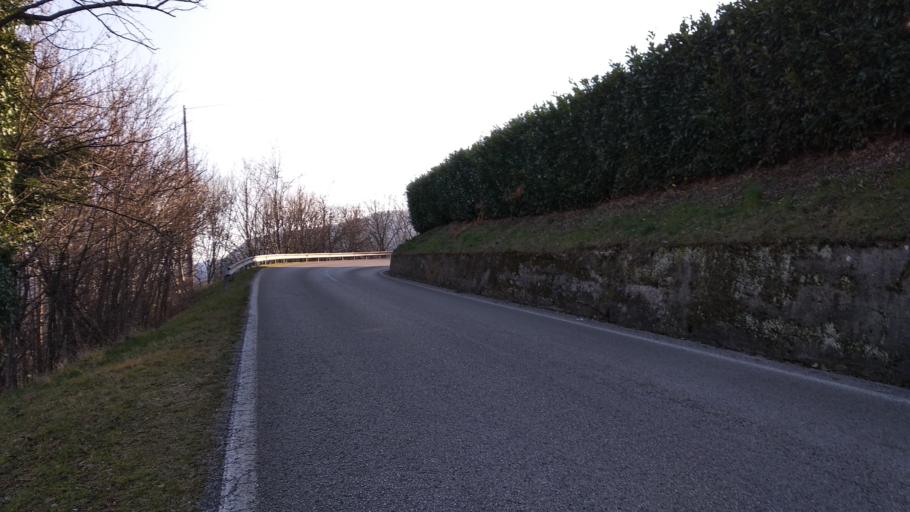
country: IT
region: Veneto
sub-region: Provincia di Vicenza
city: Monte di Malo
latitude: 45.6649
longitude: 11.3688
